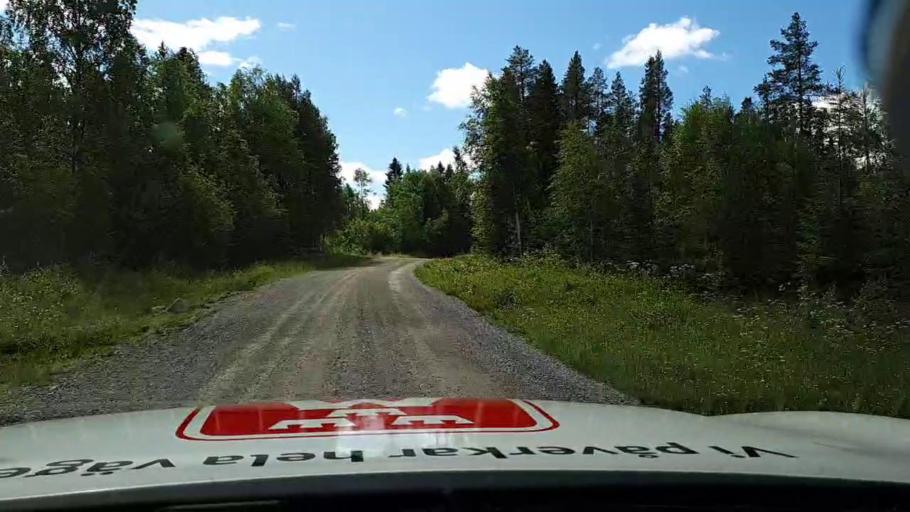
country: SE
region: Jaemtland
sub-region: Braecke Kommun
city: Braecke
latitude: 62.7461
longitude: 15.5024
